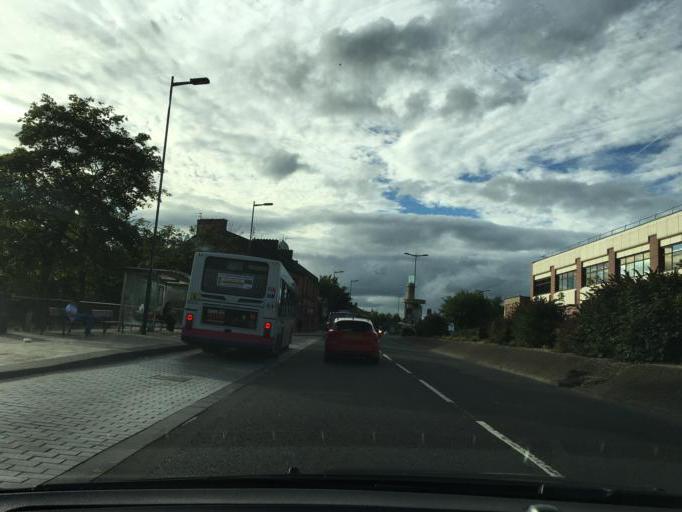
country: GB
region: Scotland
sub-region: North Lanarkshire
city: Motherwell
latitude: 55.7889
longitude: -3.9918
